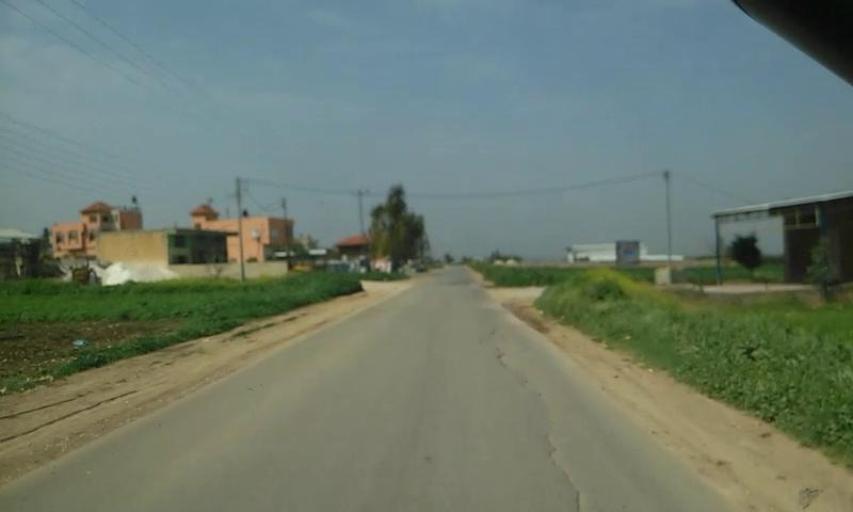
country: PS
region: West Bank
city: Kafr Dan
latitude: 32.4930
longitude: 35.2571
